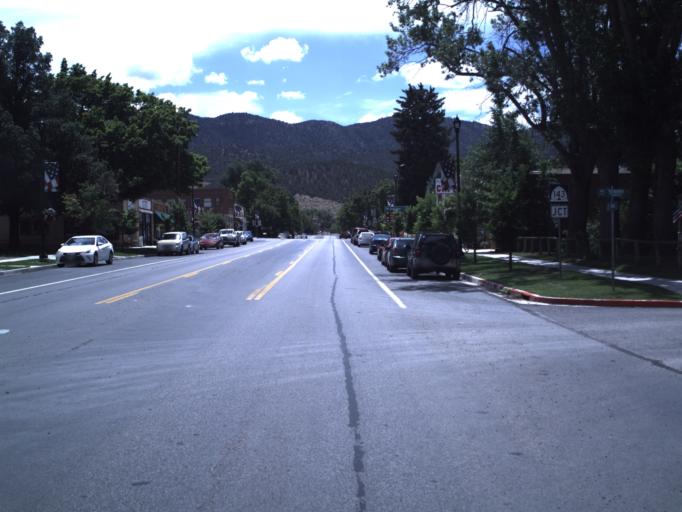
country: US
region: Utah
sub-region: Iron County
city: Parowan
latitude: 37.8436
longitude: -112.8277
